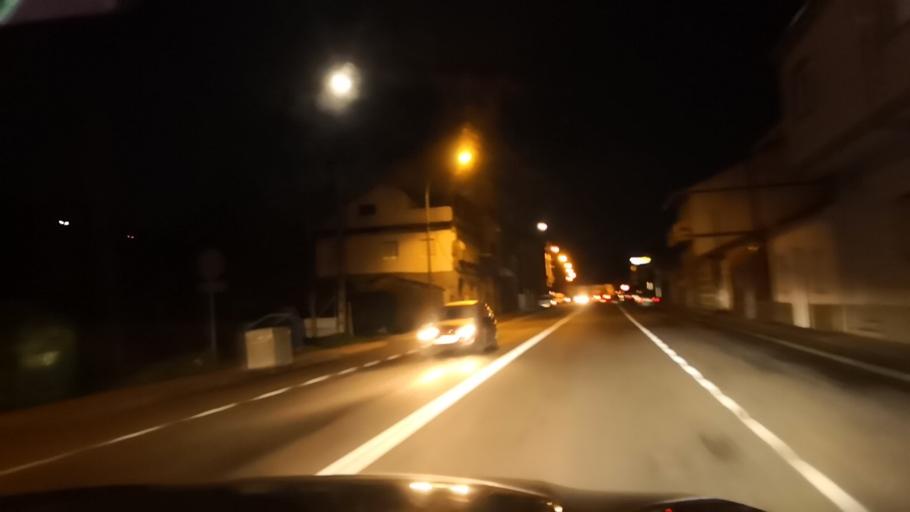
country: ES
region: Galicia
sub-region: Provincia de Ourense
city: Verin
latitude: 41.9391
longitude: -7.4526
